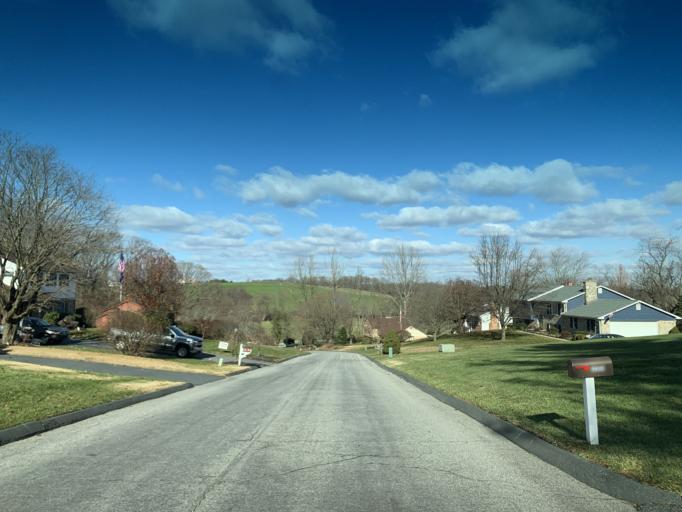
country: US
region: Maryland
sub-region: Harford County
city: South Bel Air
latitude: 39.5803
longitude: -76.2479
